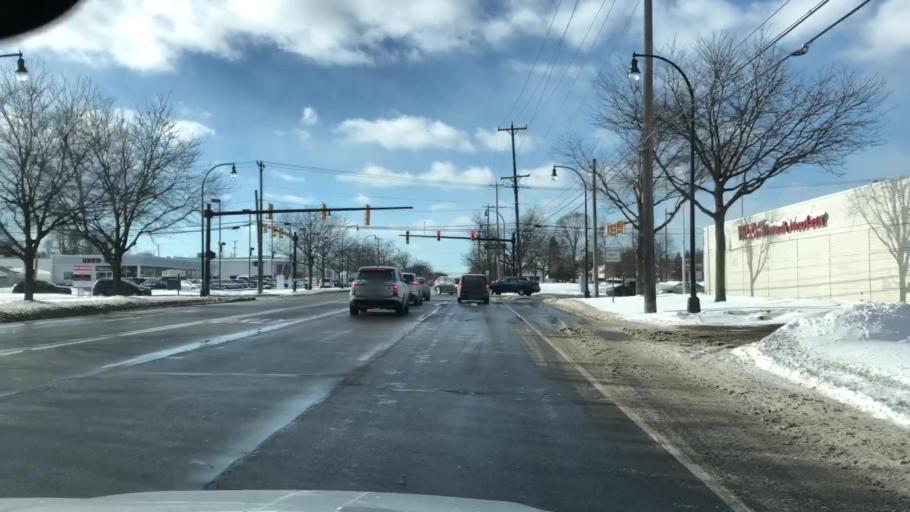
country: US
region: Michigan
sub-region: Wayne County
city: Livonia
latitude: 42.3682
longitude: -83.3812
